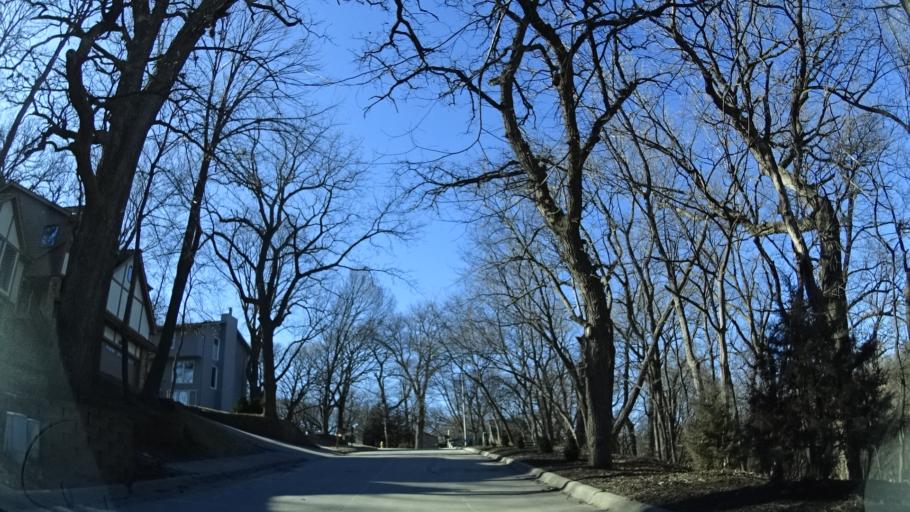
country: US
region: Nebraska
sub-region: Sarpy County
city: Bellevue
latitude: 41.1543
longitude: -95.8974
